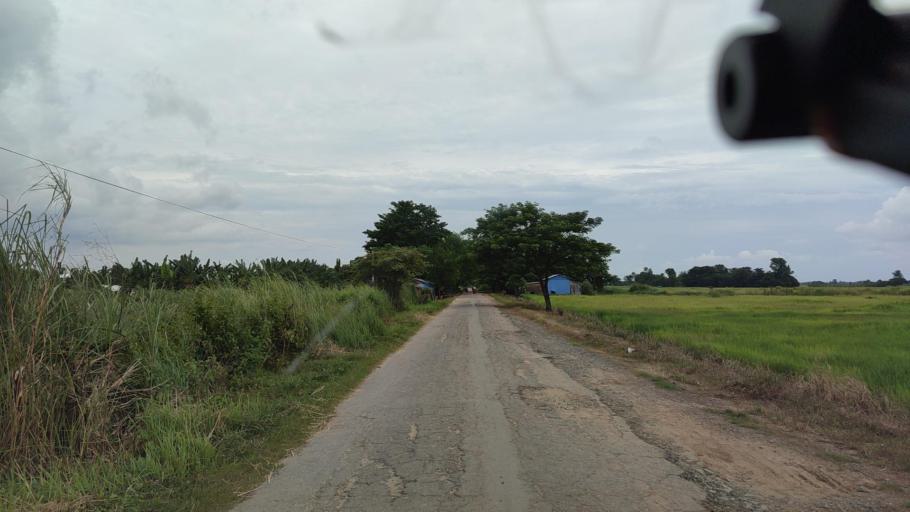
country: MM
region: Bago
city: Letpandan
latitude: 17.9710
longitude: 95.5121
